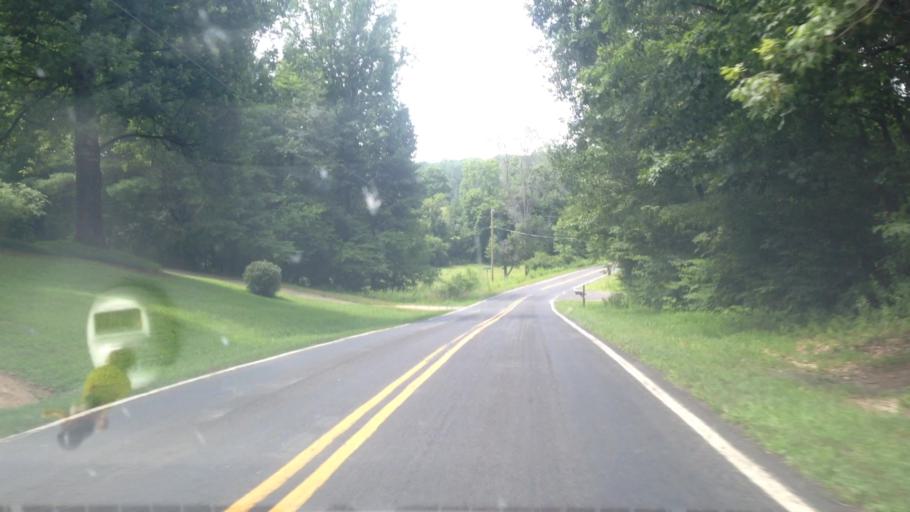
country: US
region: North Carolina
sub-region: Forsyth County
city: Walkertown
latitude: 36.2127
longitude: -80.1120
